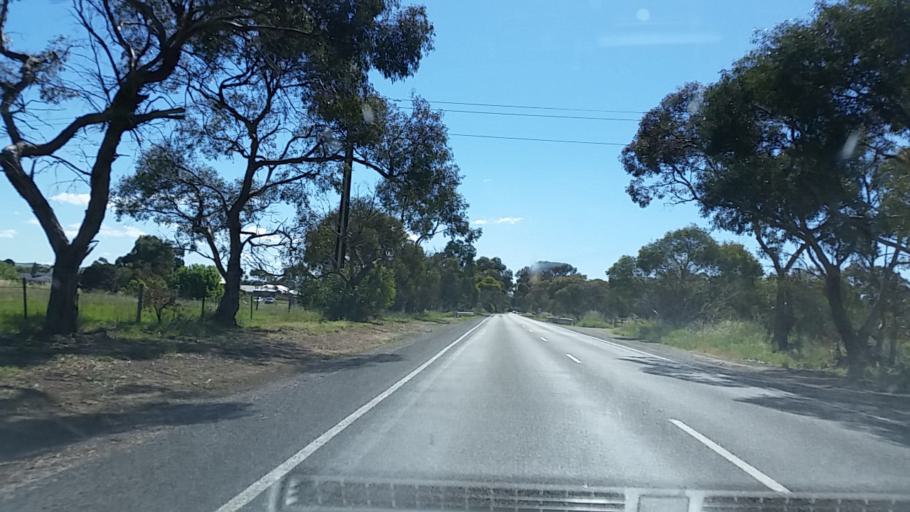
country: AU
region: South Australia
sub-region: Alexandrina
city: Strathalbyn
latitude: -35.2632
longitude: 138.9108
